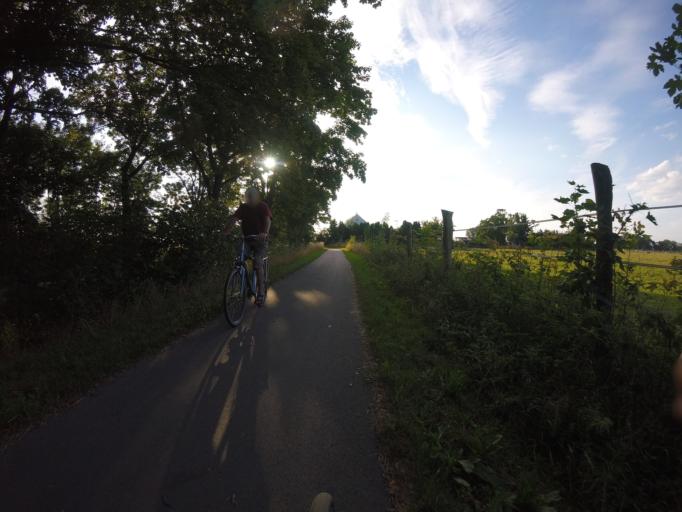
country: DE
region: Brandenburg
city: Altlandsberg
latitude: 52.5636
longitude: 13.7531
